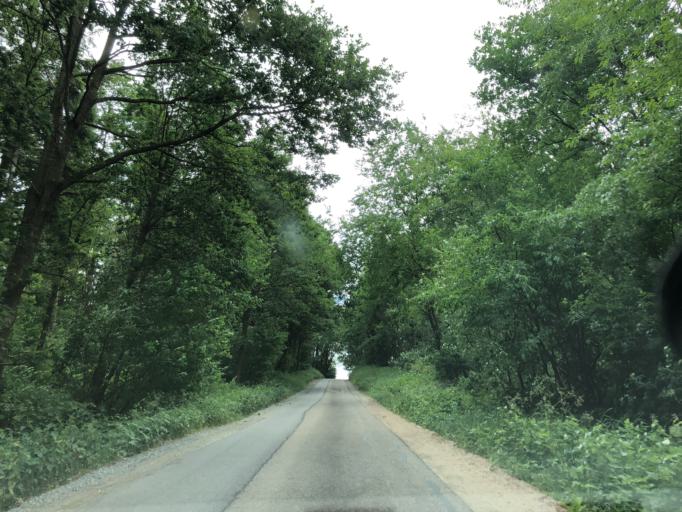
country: DK
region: Central Jutland
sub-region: Silkeborg Kommune
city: Svejbaek
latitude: 56.2102
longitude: 9.6865
